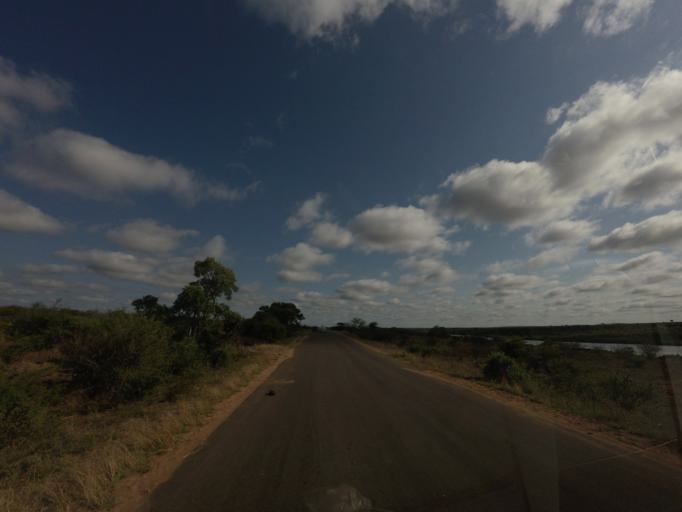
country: ZA
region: Mpumalanga
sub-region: Ehlanzeni District
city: Komatipoort
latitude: -25.1484
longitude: 31.9399
